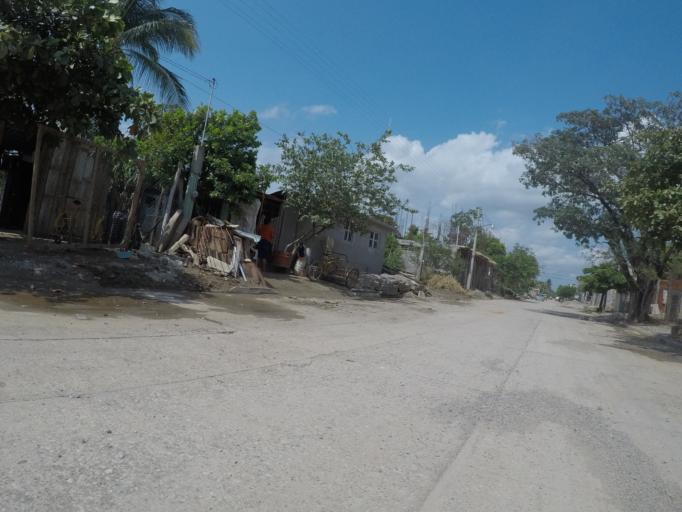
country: MX
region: Oaxaca
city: Union Hidalgo
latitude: 16.4700
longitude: -94.8310
